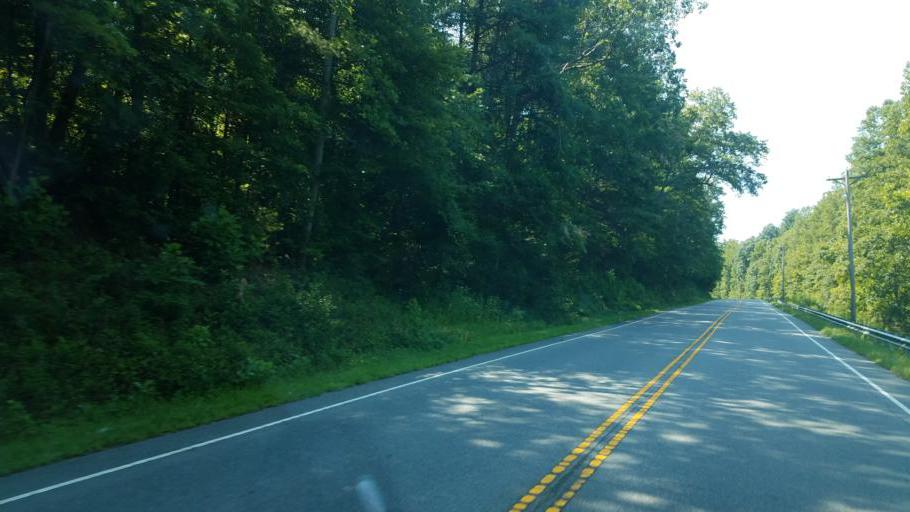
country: US
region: North Carolina
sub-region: Burke County
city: Glen Alpine
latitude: 35.8178
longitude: -81.7907
